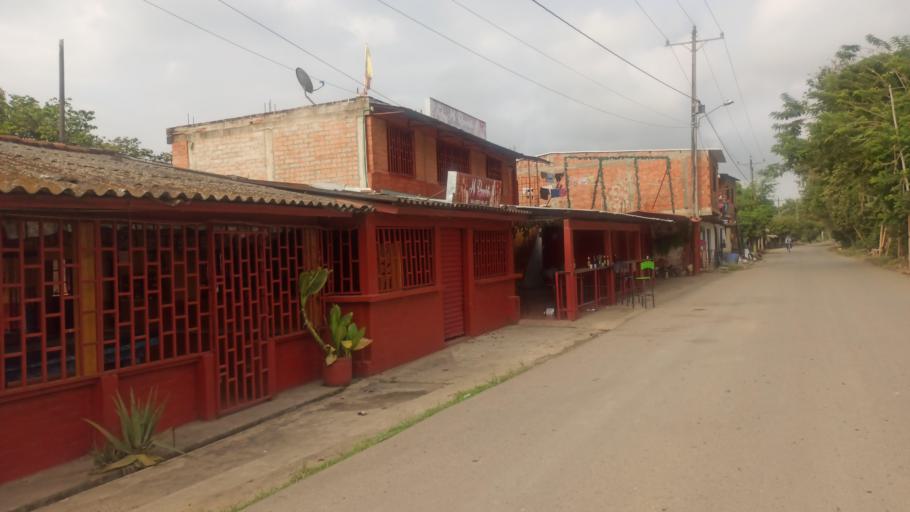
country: CO
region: Valle del Cauca
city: Jamundi
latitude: 3.2042
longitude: -76.4985
